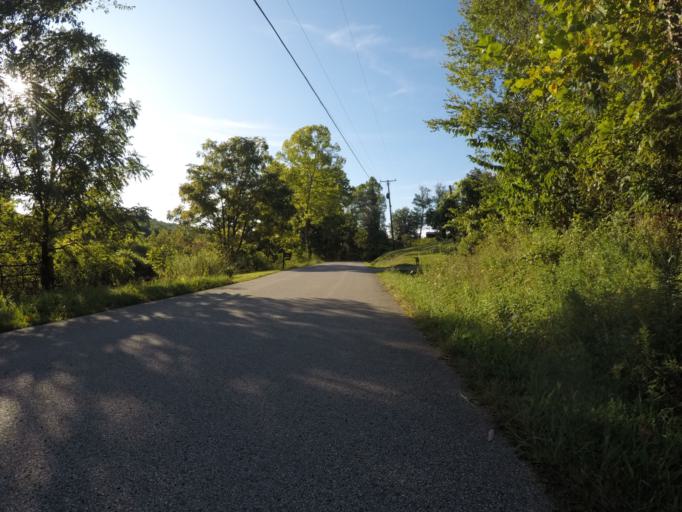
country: US
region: West Virginia
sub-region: Cabell County
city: Huntington
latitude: 38.5138
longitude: -82.4986
